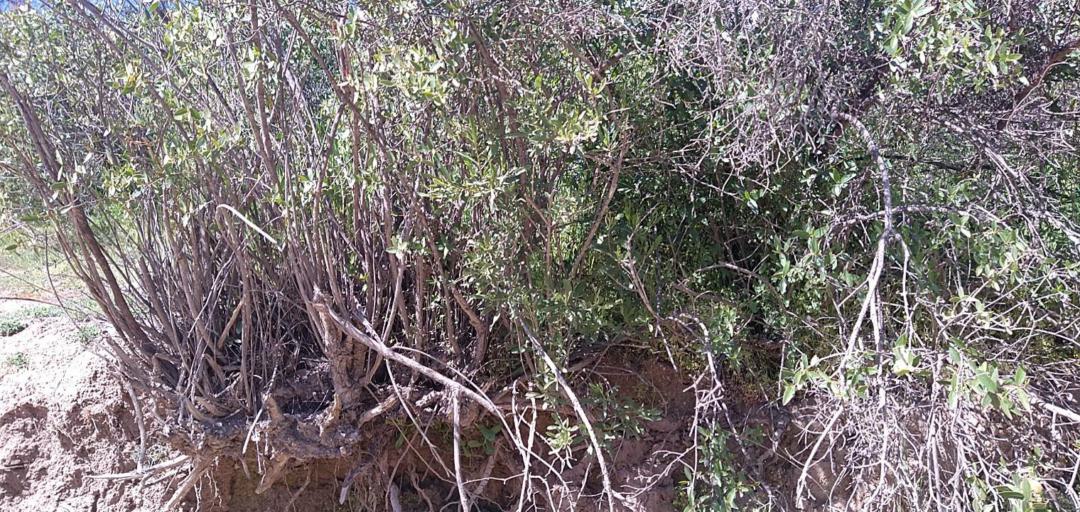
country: CL
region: Santiago Metropolitan
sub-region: Provincia de Chacabuco
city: Lampa
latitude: -33.1967
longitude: -71.0904
